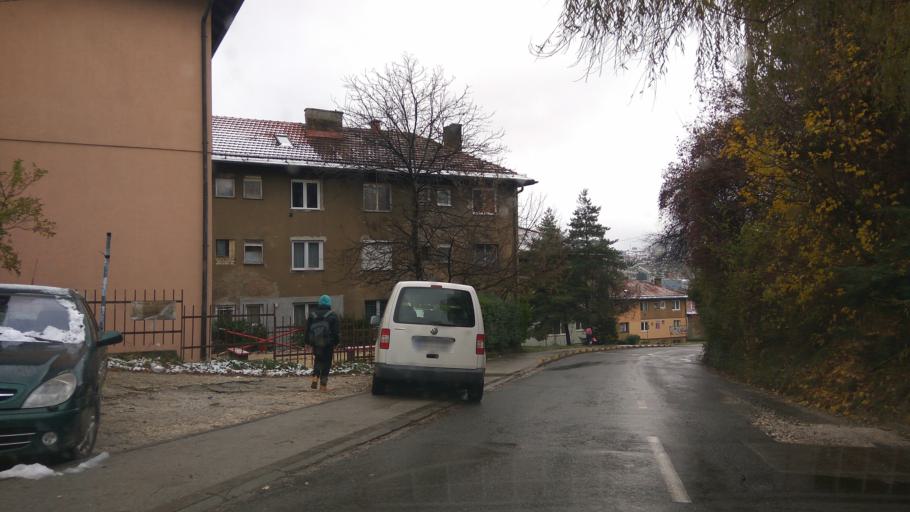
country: BA
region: Federation of Bosnia and Herzegovina
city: Kobilja Glava
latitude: 43.8700
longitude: 18.4067
